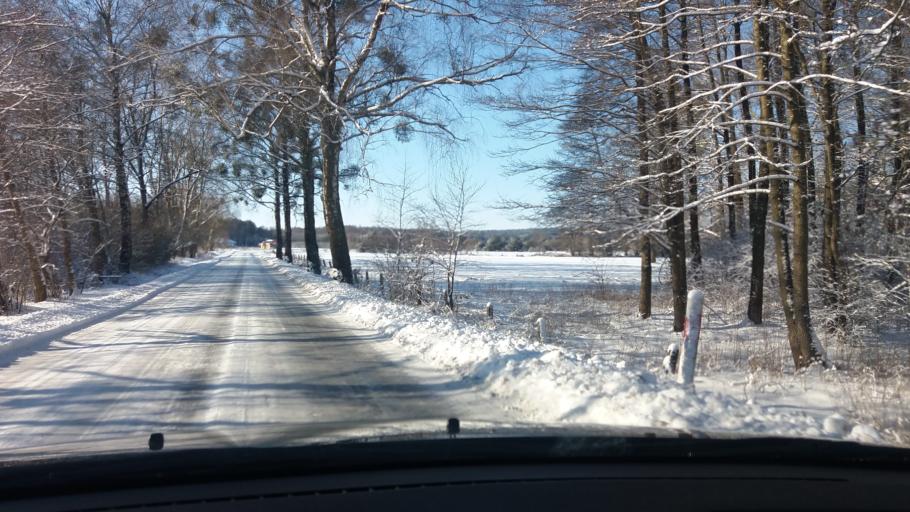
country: PL
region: Masovian Voivodeship
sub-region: Powiat mlawski
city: Dzierzgowo
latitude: 53.3339
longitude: 20.6278
